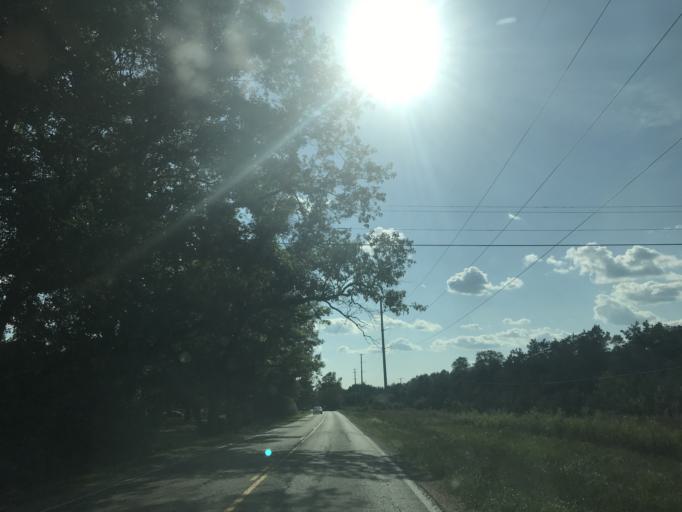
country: US
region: Michigan
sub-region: Newaygo County
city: Newaygo
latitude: 43.4286
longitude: -85.7548
